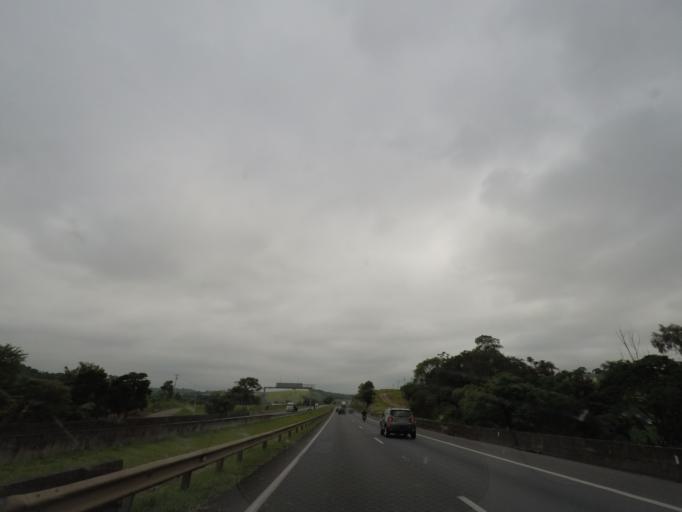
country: BR
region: Sao Paulo
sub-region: Itatiba
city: Itatiba
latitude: -23.0167
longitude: -46.7589
